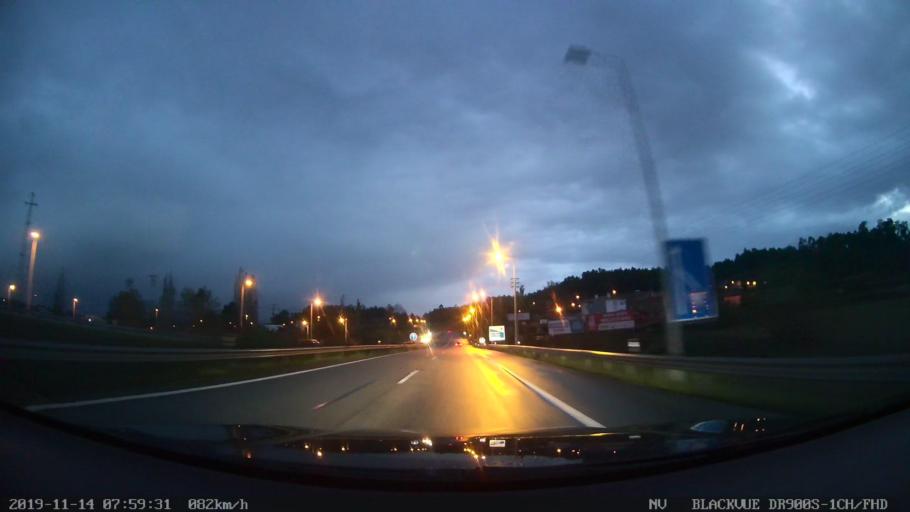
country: PT
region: Braga
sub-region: Braga
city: Oliveira
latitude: 41.5076
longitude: -8.4454
